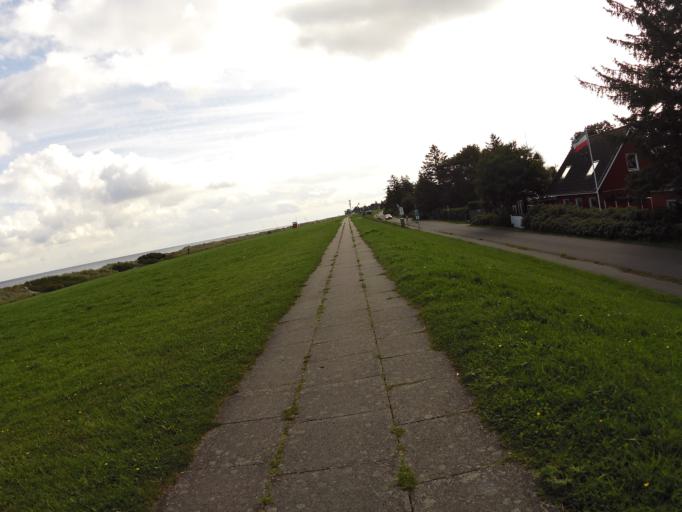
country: DE
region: Schleswig-Holstein
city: Wisch
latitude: 54.4305
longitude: 10.3584
